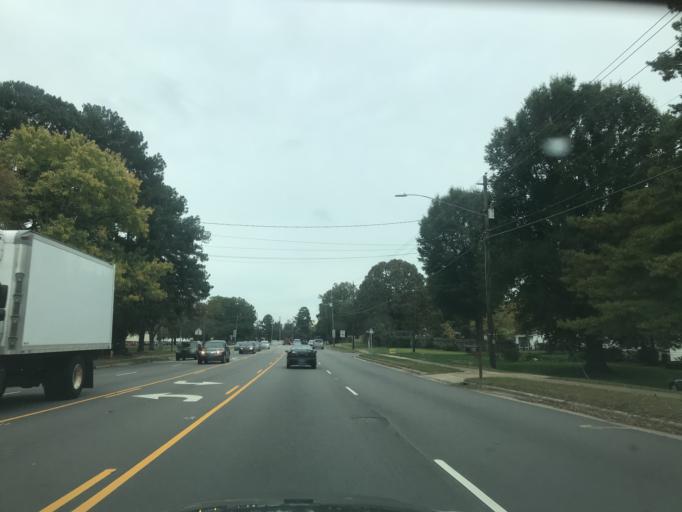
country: US
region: North Carolina
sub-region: Wake County
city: West Raleigh
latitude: 35.8550
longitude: -78.6153
